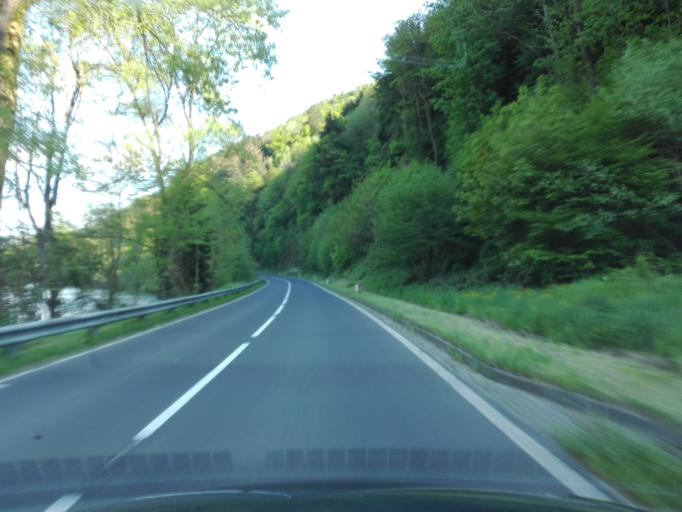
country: AT
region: Upper Austria
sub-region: Politischer Bezirk Rohrbach
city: Pfarrkirchen im Muehlkreis
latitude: 48.4686
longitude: 13.7757
